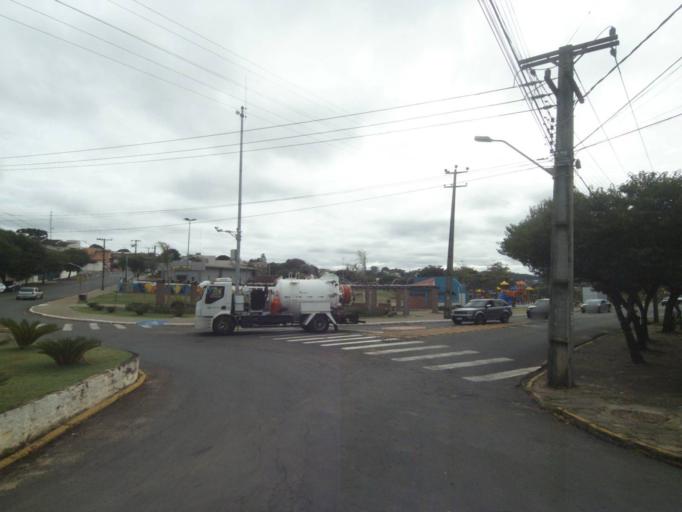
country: BR
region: Parana
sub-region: Telemaco Borba
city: Telemaco Borba
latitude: -24.3348
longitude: -50.6208
